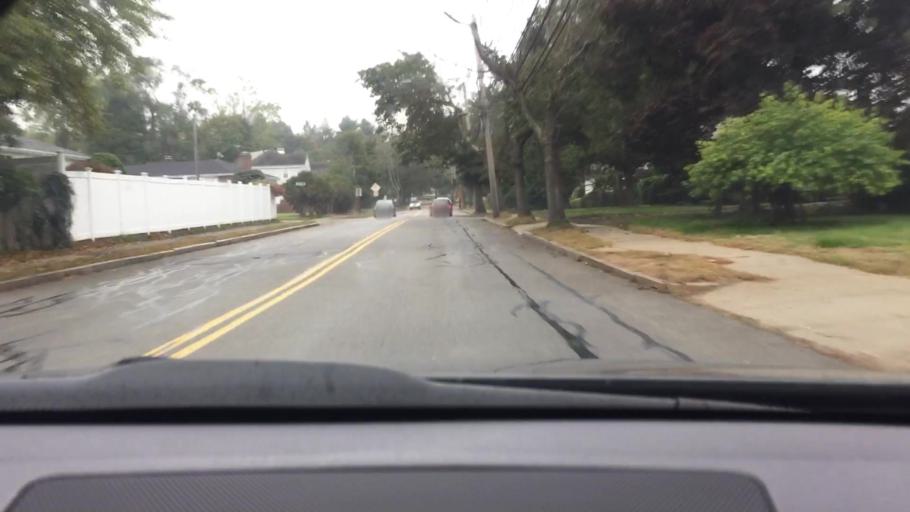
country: US
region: Massachusetts
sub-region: Middlesex County
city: Newton
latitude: 42.3117
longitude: -71.1967
